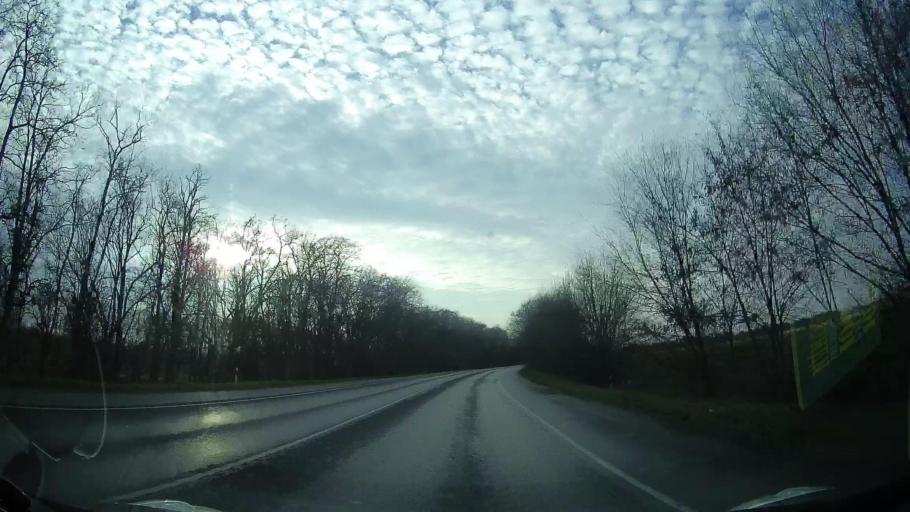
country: RU
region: Rostov
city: Bagayevskaya
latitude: 47.1632
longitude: 40.2604
